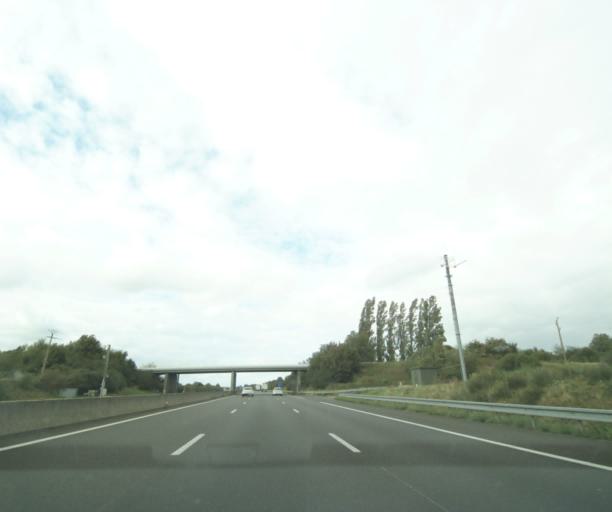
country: FR
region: Ile-de-France
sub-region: Departement de l'Essonne
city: Corbreuse
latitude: 48.5226
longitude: 1.9082
